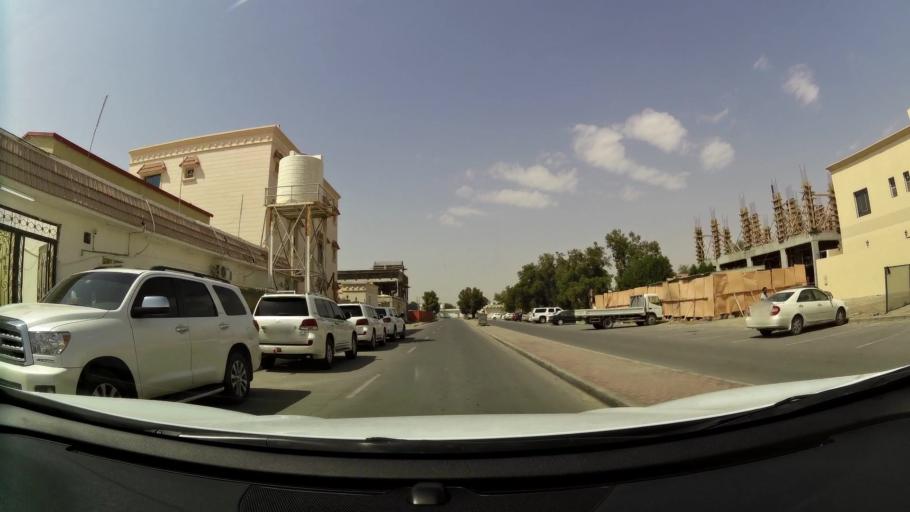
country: AE
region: Abu Dhabi
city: Abu Dhabi
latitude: 24.2885
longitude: 54.6416
